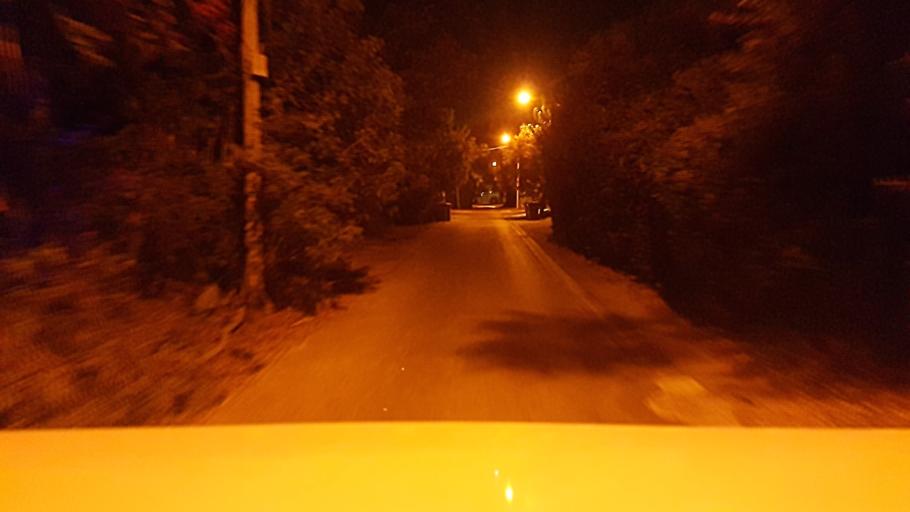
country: IL
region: Central District
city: Nehalim
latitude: 32.0760
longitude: 34.9167
